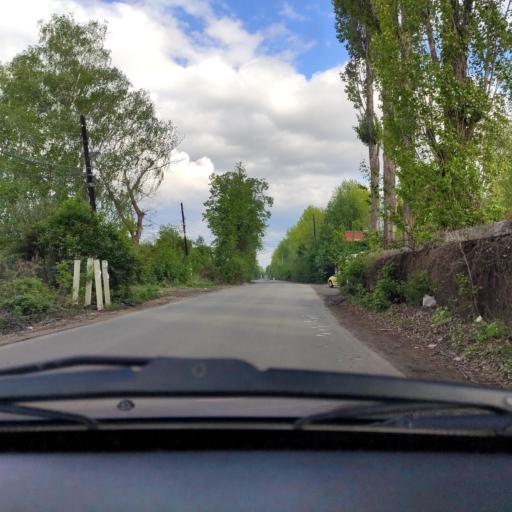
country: RU
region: Voronezj
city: Voronezh
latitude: 51.5987
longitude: 39.1679
